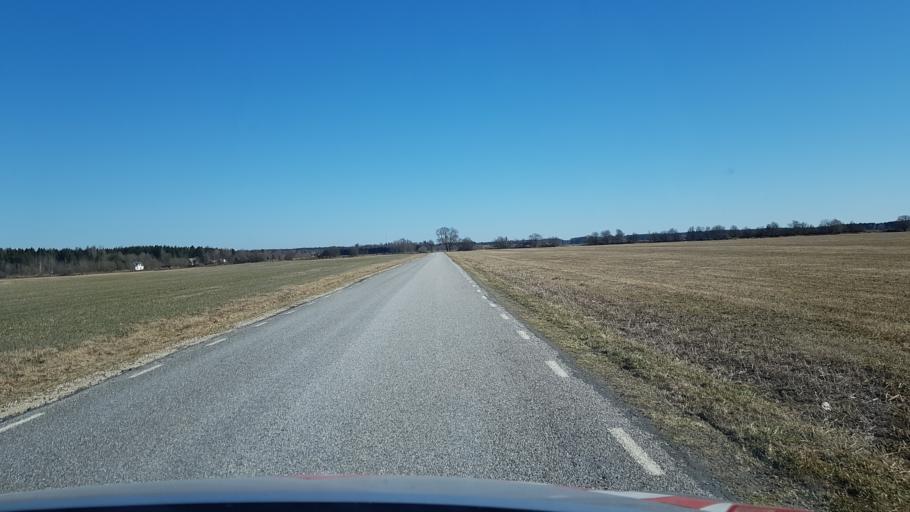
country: EE
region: Laeaene-Virumaa
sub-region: Viru-Nigula vald
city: Kunda
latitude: 59.4053
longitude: 26.5393
